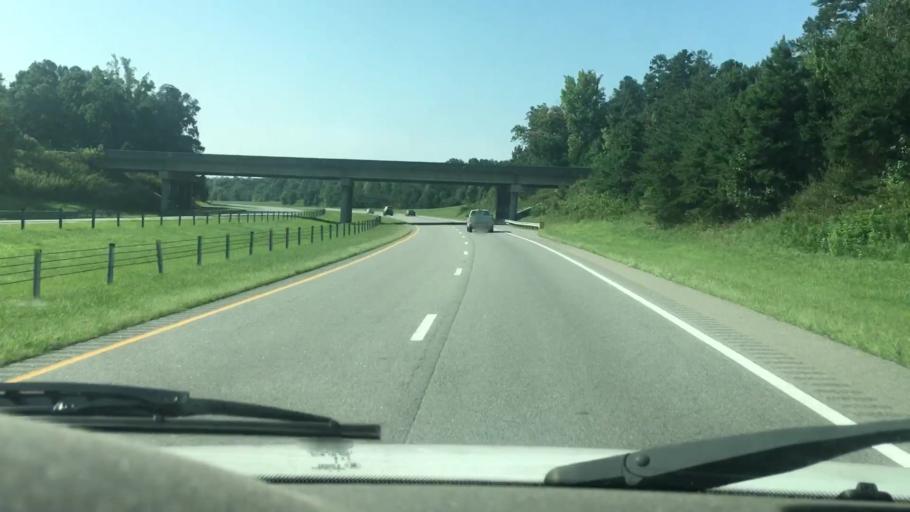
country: US
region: North Carolina
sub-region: Lincoln County
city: Lowesville
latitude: 35.3837
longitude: -81.0011
